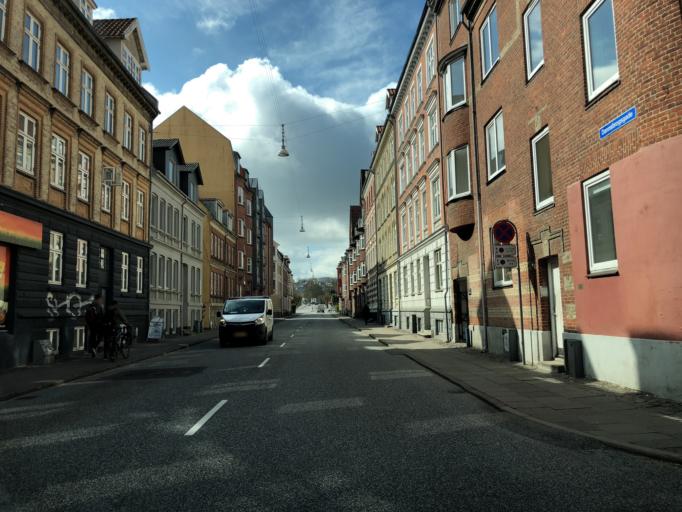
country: DK
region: North Denmark
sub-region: Alborg Kommune
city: Aalborg
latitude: 57.0517
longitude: 9.9041
